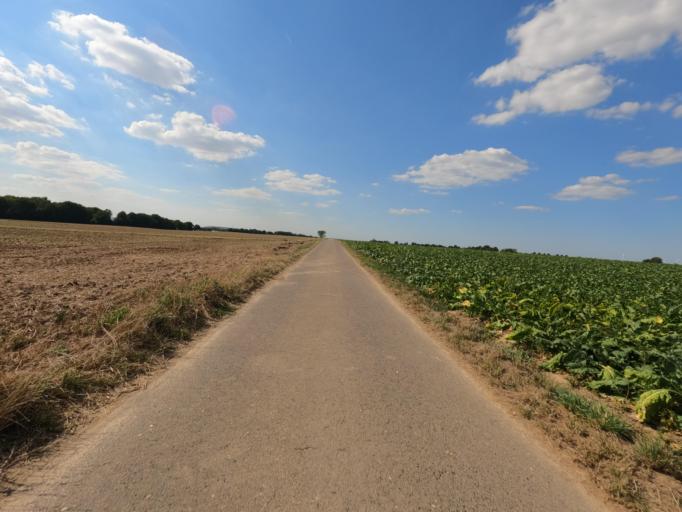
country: DE
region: North Rhine-Westphalia
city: Erkelenz
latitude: 51.0835
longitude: 6.2721
